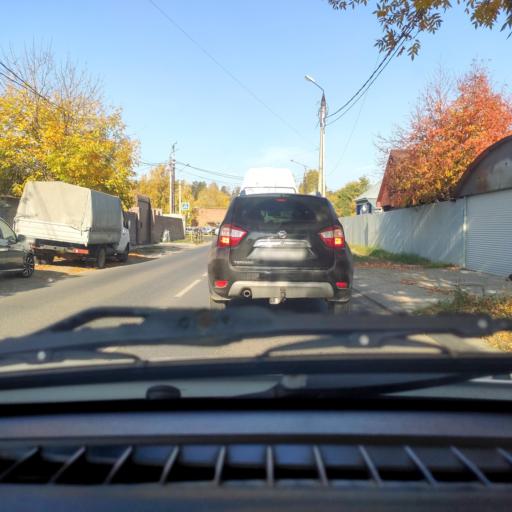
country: RU
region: Samara
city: Tol'yatti
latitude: 53.5095
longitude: 49.3960
